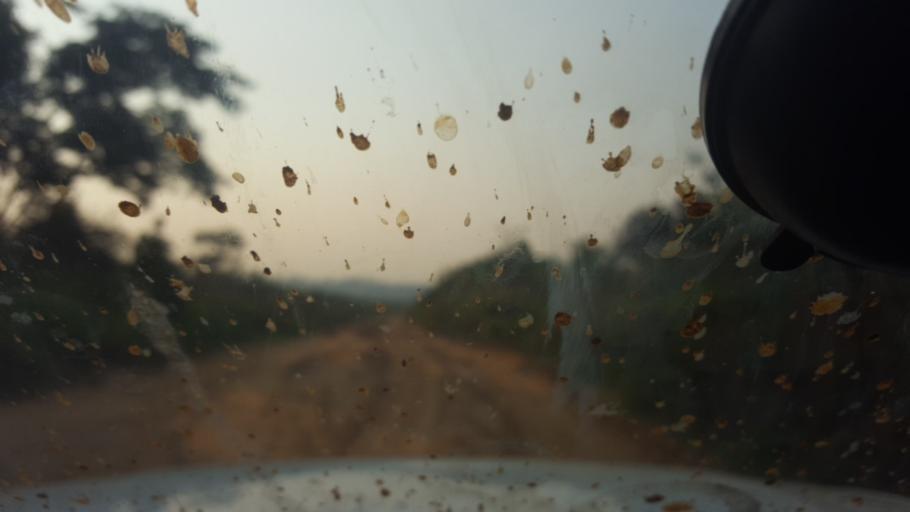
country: CD
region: Bandundu
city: Mushie
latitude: -3.7522
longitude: 16.6656
